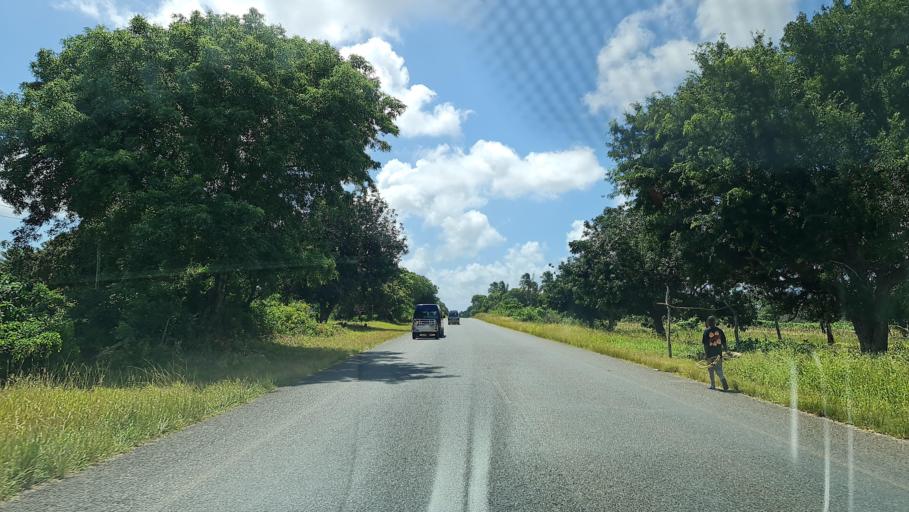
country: MZ
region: Inhambane
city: Maxixe
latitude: -24.5407
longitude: 34.9222
